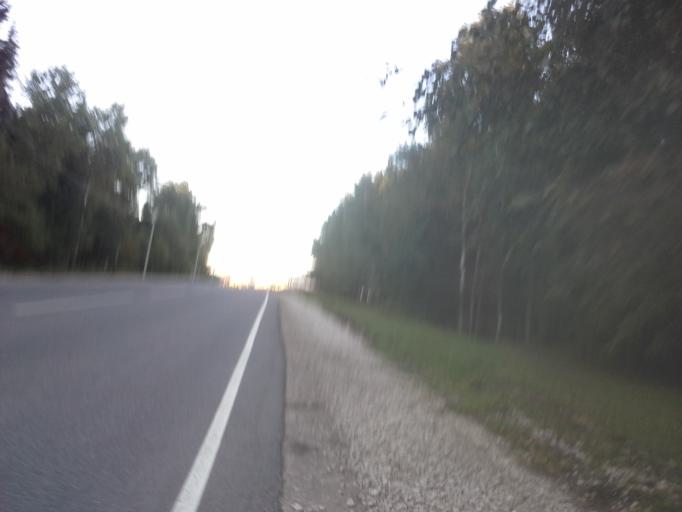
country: RU
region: Moskovskaya
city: Kievskij
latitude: 55.4851
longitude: 36.9120
